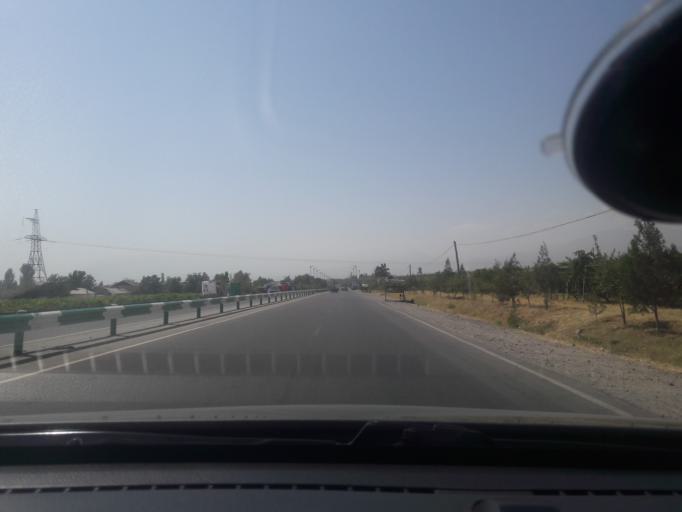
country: TJ
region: Republican Subordination
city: Hisor
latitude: 38.5602
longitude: 68.4531
